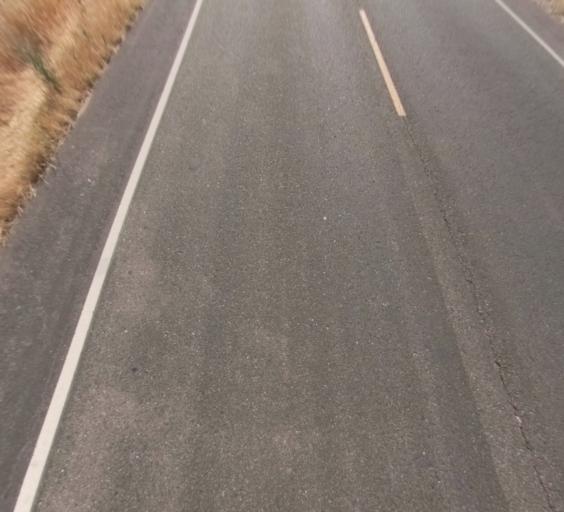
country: US
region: California
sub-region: Madera County
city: Parksdale
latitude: 36.9670
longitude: -120.0002
